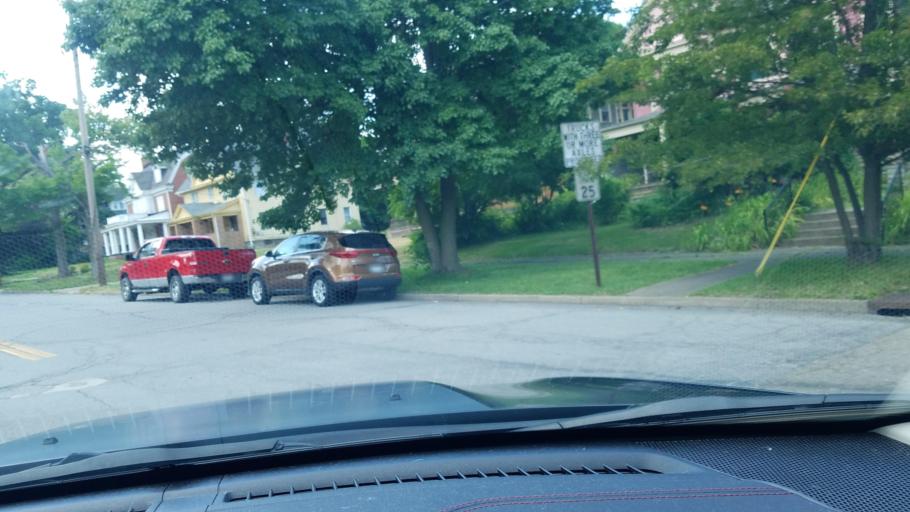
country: US
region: Ohio
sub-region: Mahoning County
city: Youngstown
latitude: 41.1163
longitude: -80.6456
